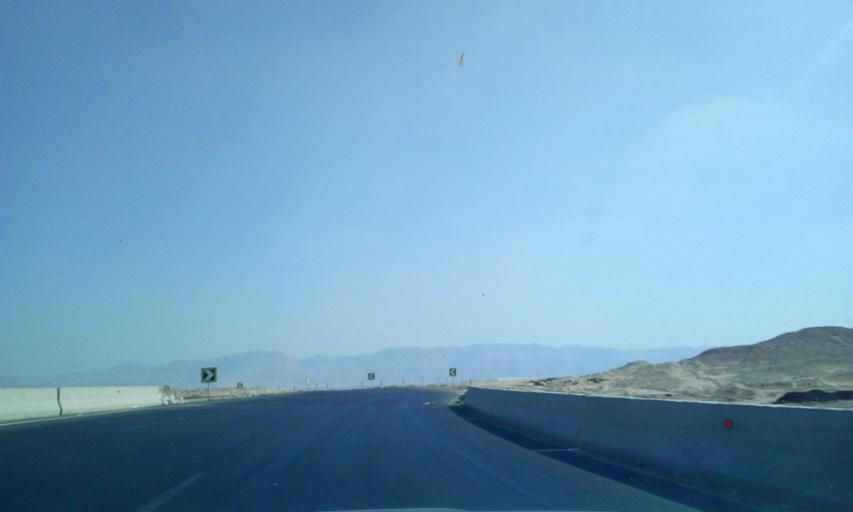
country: EG
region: As Suways
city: Ain Sukhna
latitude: 29.6660
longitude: 32.2347
